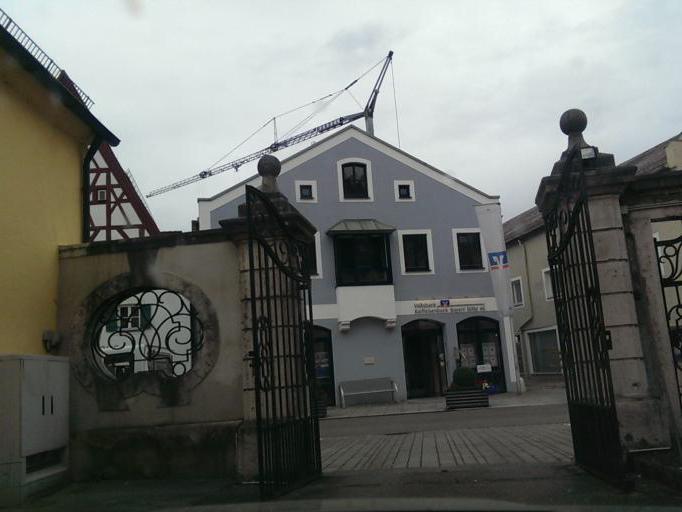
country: DE
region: Bavaria
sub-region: Upper Palatinate
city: Berching
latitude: 49.0342
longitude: 11.4748
